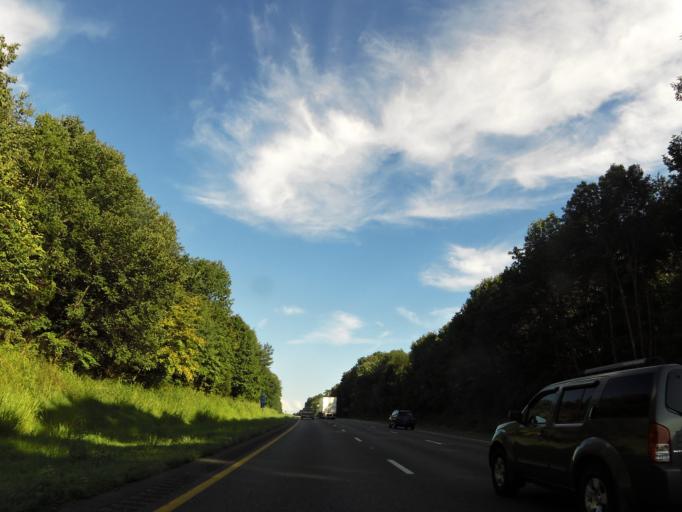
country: US
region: Tennessee
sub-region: Montgomery County
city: Clarksville
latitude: 36.5360
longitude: -87.2359
